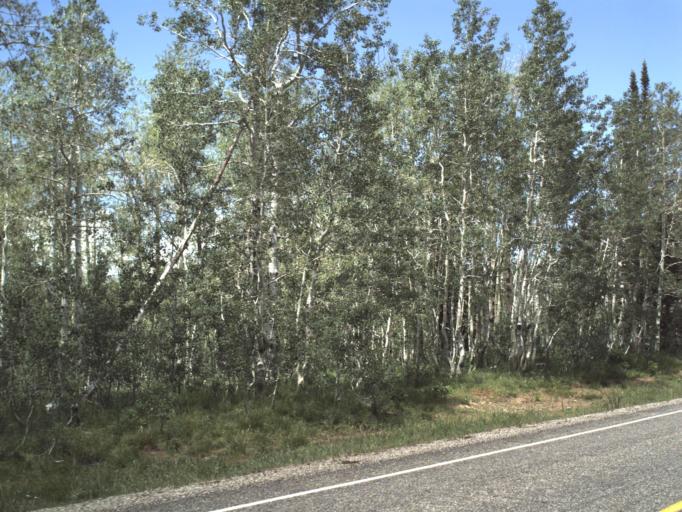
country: US
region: Utah
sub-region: Weber County
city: Wolf Creek
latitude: 41.4677
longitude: -111.4919
